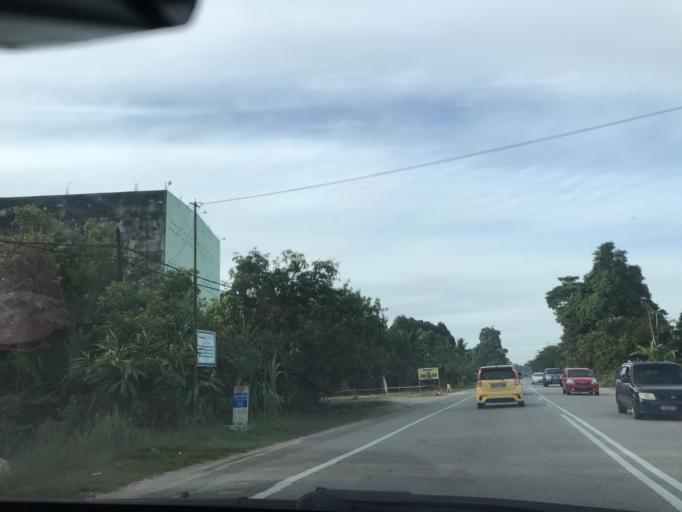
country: MY
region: Kelantan
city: Kampung Lemal
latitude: 5.9929
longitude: 102.1888
